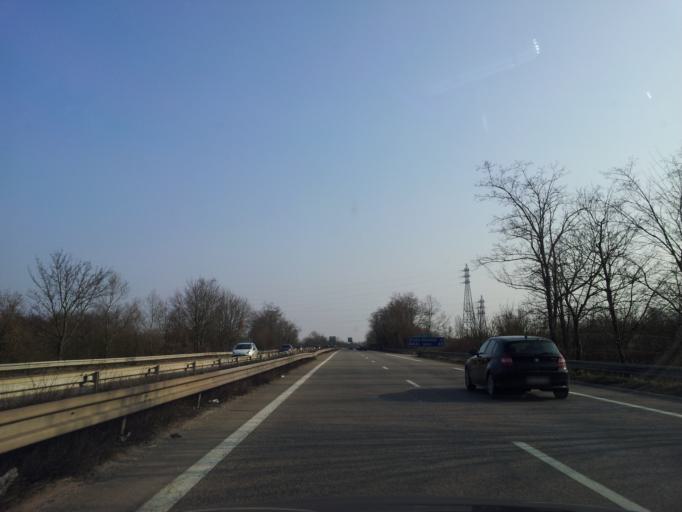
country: FR
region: Alsace
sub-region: Departement du Haut-Rhin
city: Rixheim
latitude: 47.7689
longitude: 7.4135
